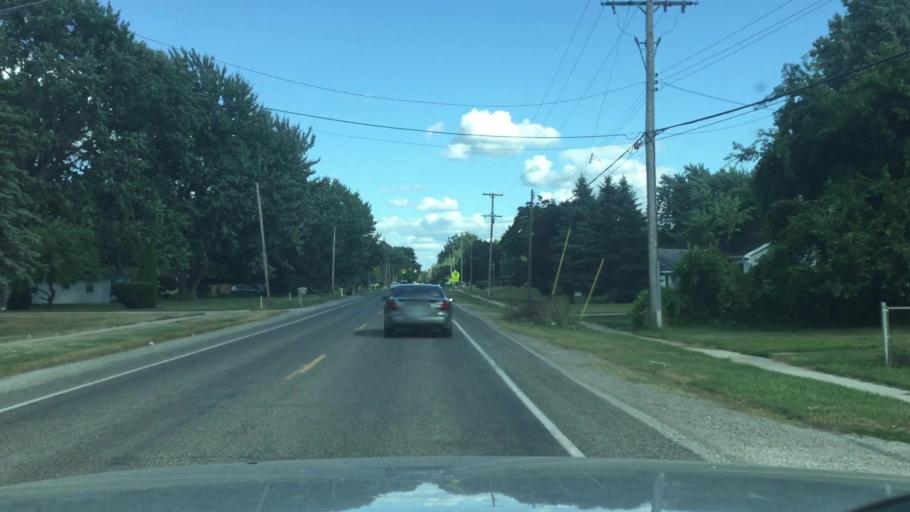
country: US
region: Michigan
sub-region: Saginaw County
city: Bridgeport
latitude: 43.3727
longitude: -83.9063
